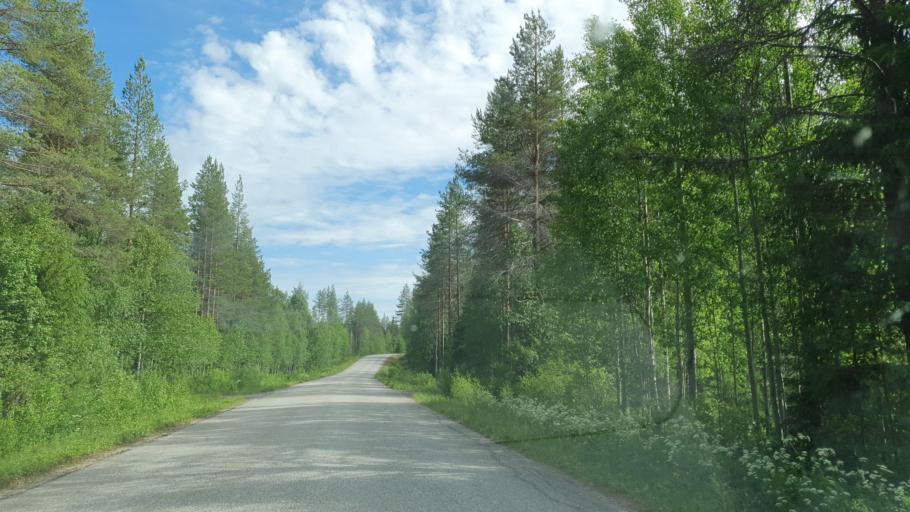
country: FI
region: Kainuu
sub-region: Kehys-Kainuu
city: Suomussalmi
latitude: 64.5847
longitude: 29.1182
